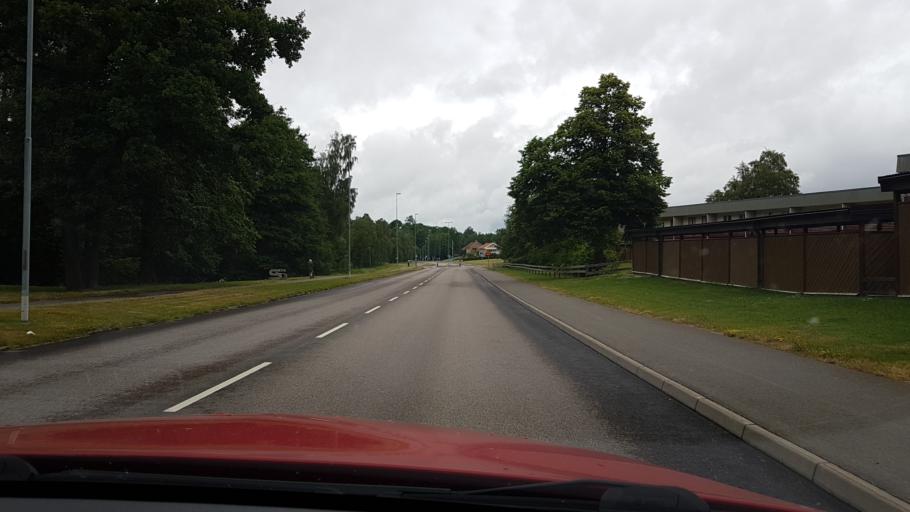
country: SE
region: Vaestra Goetaland
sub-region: Skovde Kommun
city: Skultorp
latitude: 58.3711
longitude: 13.8294
